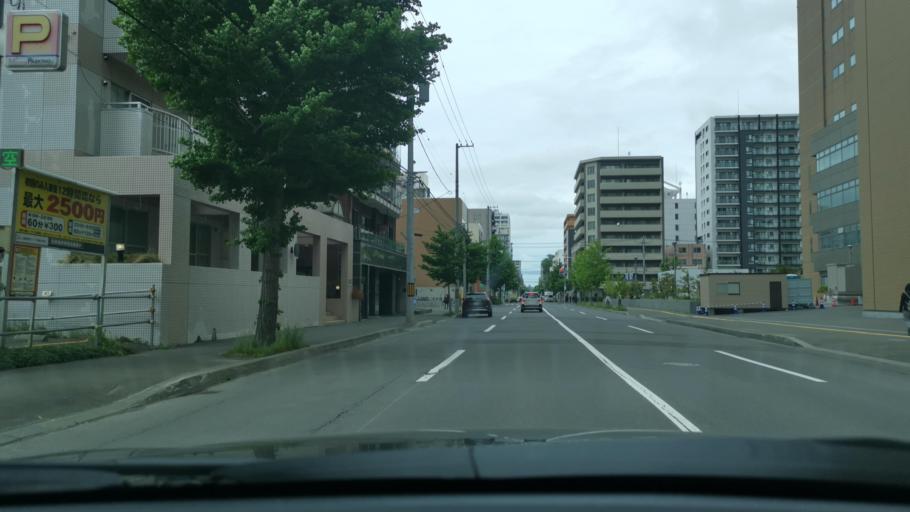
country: JP
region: Hokkaido
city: Sapporo
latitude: 43.0548
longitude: 141.3309
